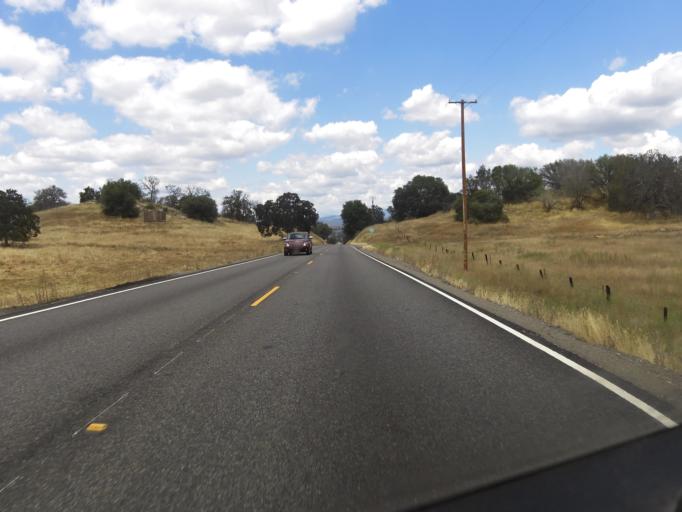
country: US
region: California
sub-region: Madera County
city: Yosemite Lakes
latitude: 37.1392
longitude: -119.7334
